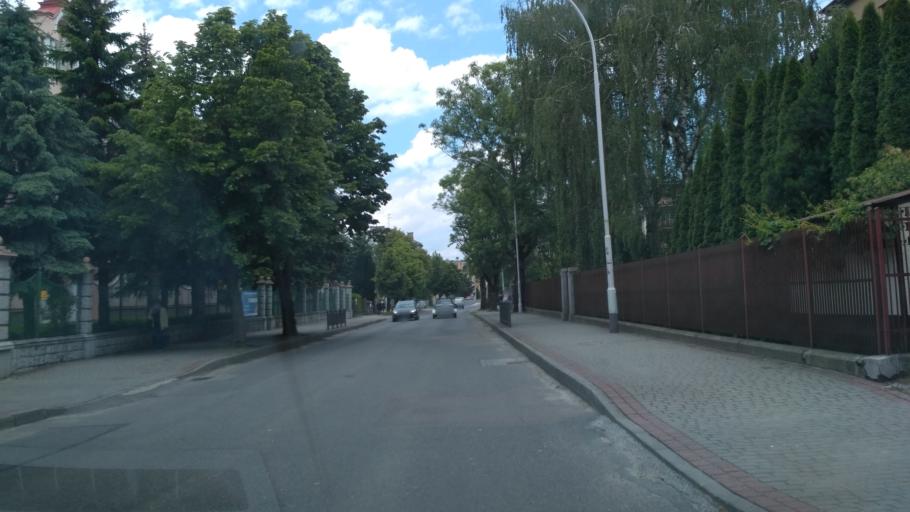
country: PL
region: Subcarpathian Voivodeship
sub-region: Przemysl
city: Przemysl
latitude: 49.7884
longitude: 22.7708
